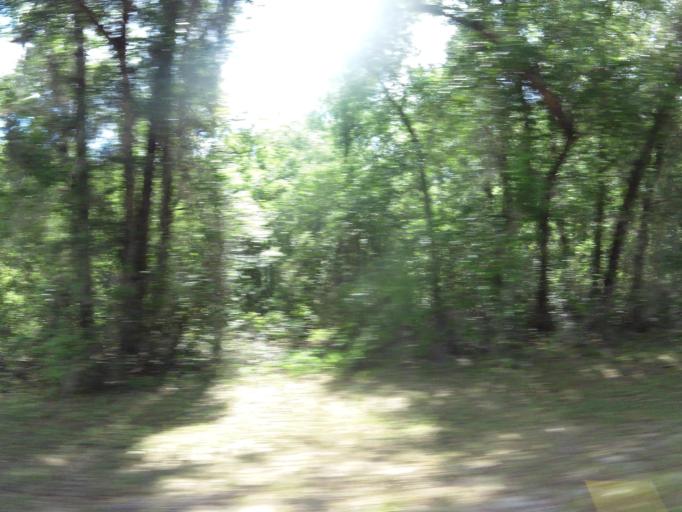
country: US
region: Florida
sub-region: Clay County
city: Keystone Heights
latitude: 29.8141
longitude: -81.9224
